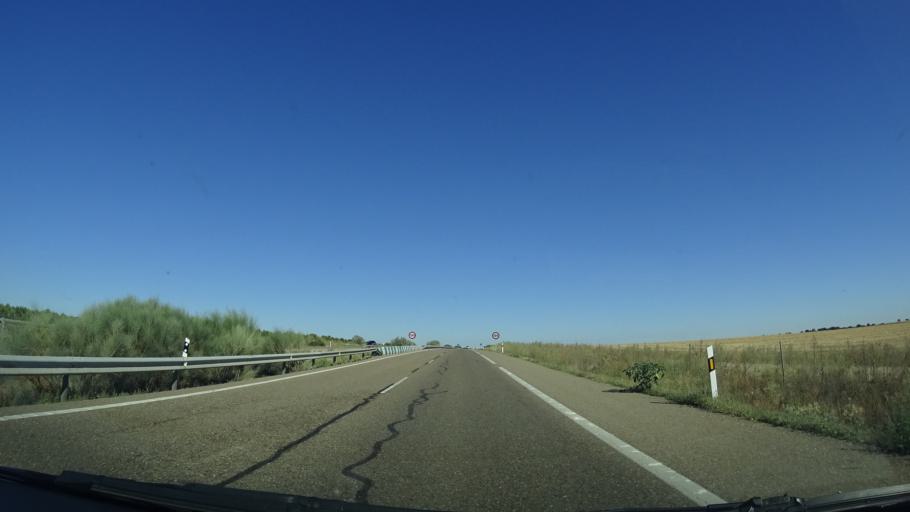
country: ES
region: Castille and Leon
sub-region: Provincia de Zamora
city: Quintanilla del Monte
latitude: 41.8199
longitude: -5.3689
